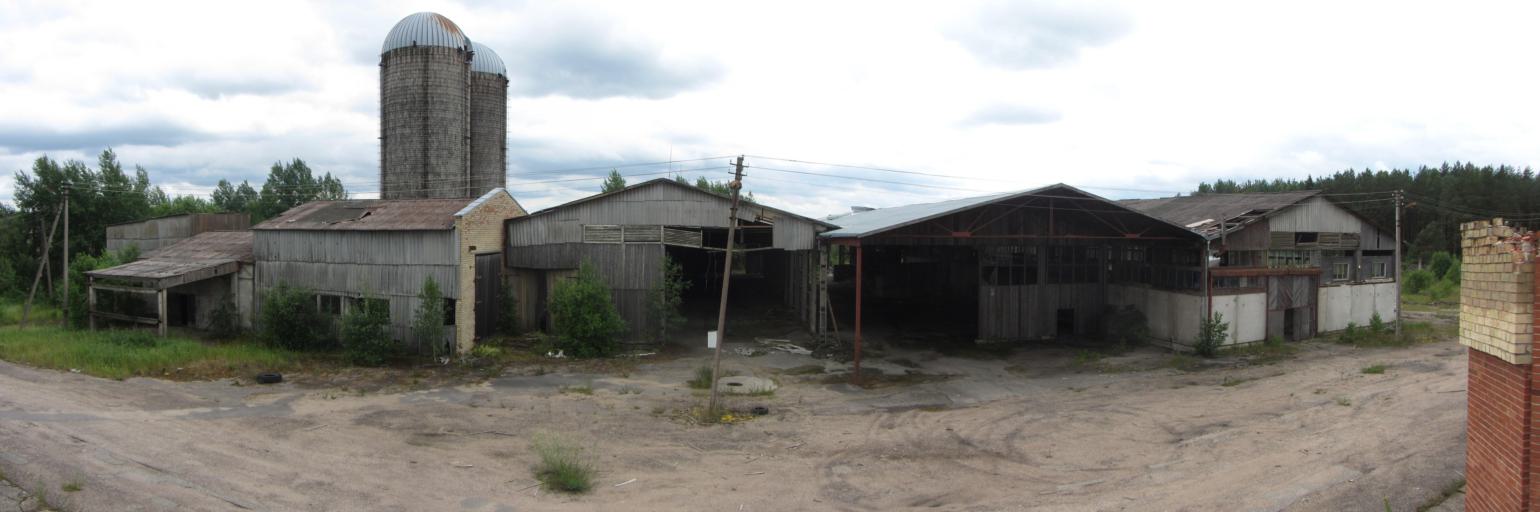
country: LT
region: Vilnius County
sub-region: Trakai
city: Rudiskes
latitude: 54.4574
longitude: 24.9617
